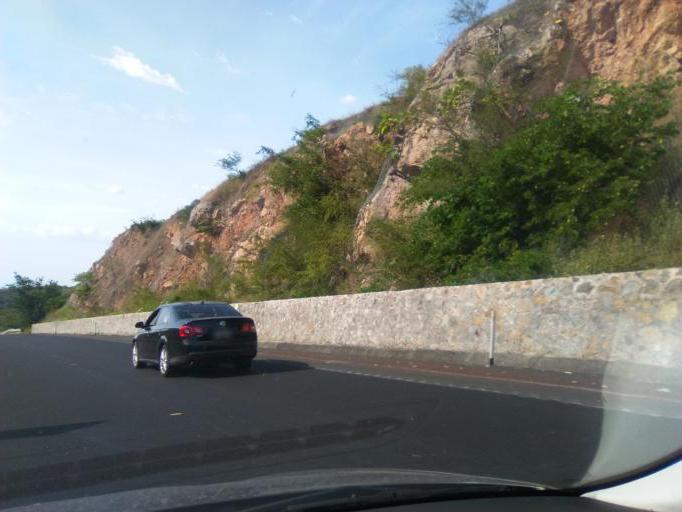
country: MX
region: Morelos
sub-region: Jojutla
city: Higueron
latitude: 18.4929
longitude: -99.1825
